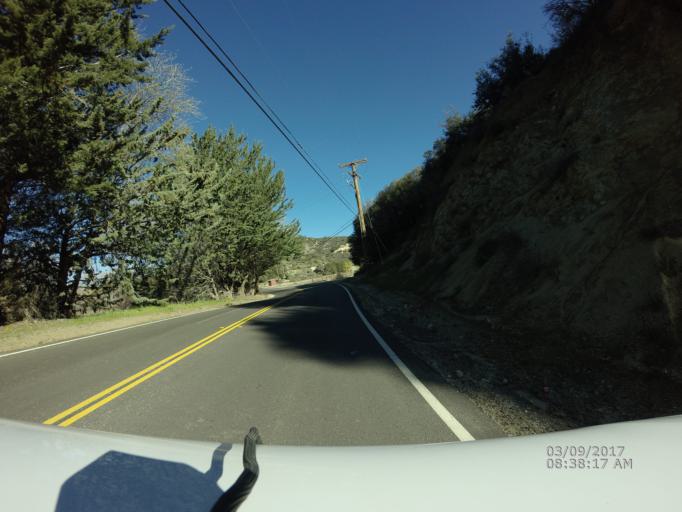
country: US
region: California
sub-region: Los Angeles County
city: Green Valley
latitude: 34.6802
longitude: -118.4547
